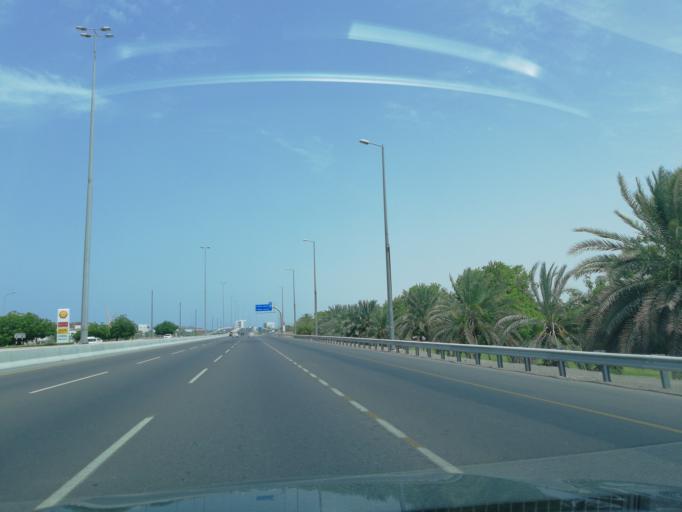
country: OM
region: Muhafazat Masqat
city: As Sib al Jadidah
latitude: 23.6564
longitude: 58.1987
